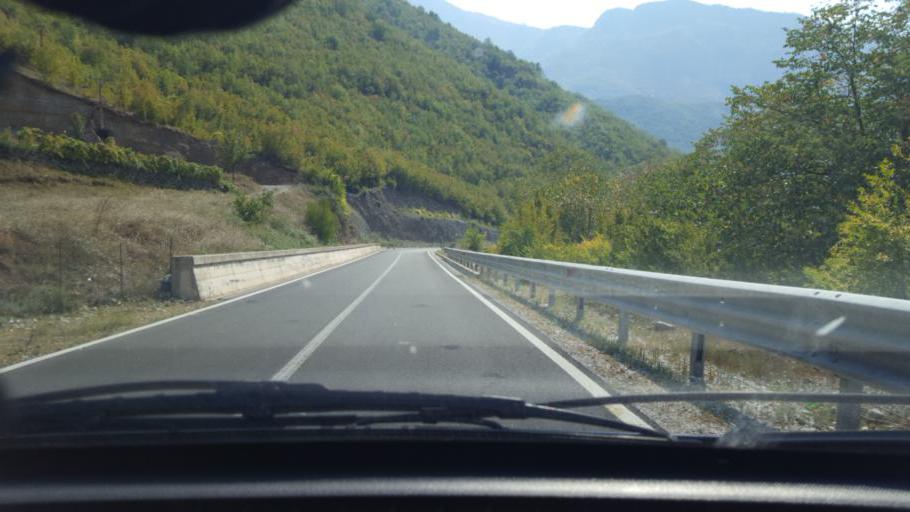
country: AL
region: Shkoder
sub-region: Rrethi i Malesia e Madhe
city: Kastrat
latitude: 42.4388
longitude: 19.5385
